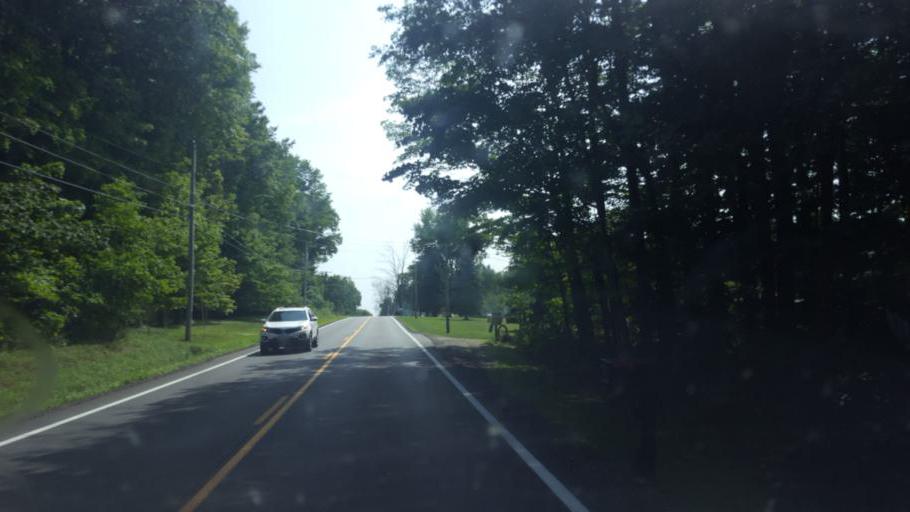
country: US
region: Ohio
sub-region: Richland County
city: Ontario
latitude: 40.7694
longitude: -82.6559
